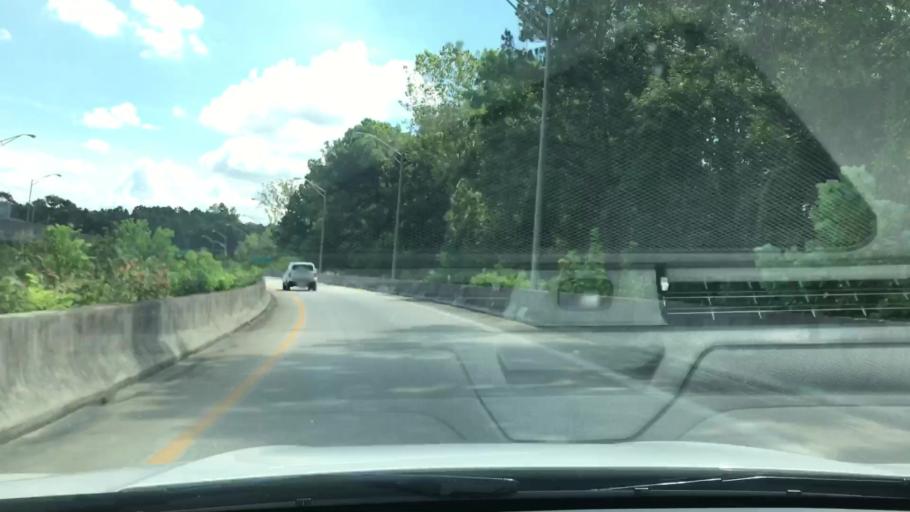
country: US
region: South Carolina
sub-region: Charleston County
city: North Charleston
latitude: 32.8931
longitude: -79.9884
